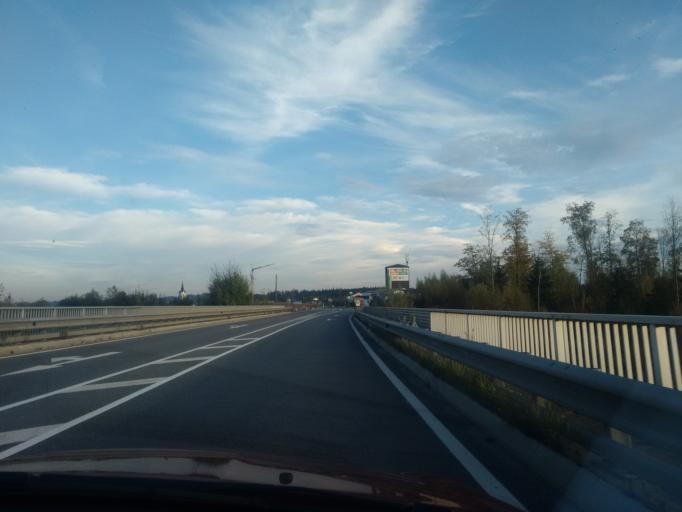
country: AT
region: Upper Austria
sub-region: Wels-Land
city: Offenhausen
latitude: 48.1827
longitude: 13.7872
